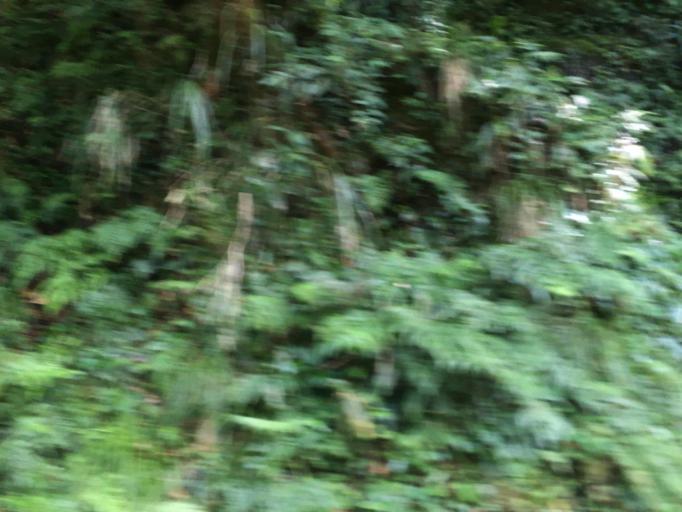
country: TW
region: Taiwan
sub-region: Yilan
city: Yilan
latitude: 24.6207
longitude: 121.4803
